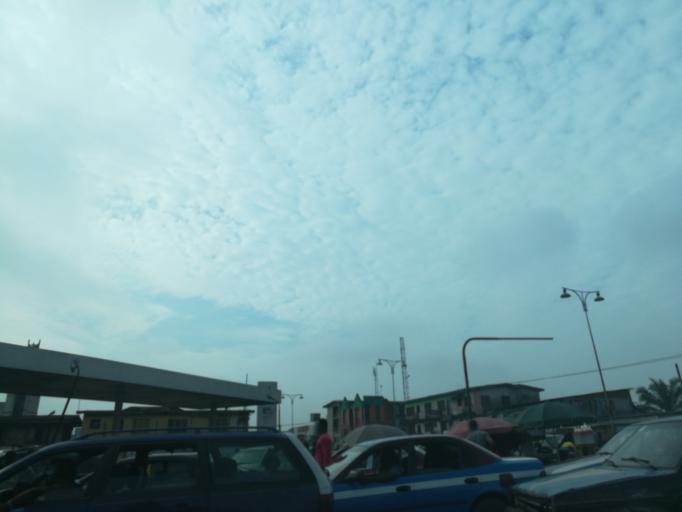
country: NG
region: Rivers
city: Port Harcourt
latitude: 4.7987
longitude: 6.9924
